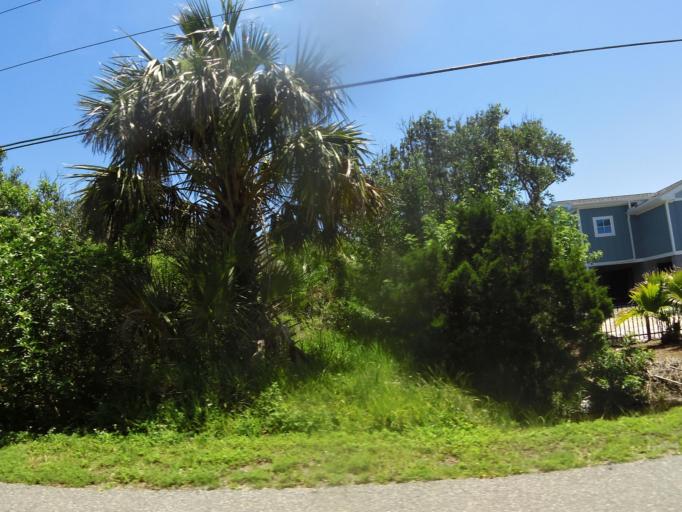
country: US
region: Florida
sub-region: Saint Johns County
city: Butler Beach
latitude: 29.7655
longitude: -81.2537
